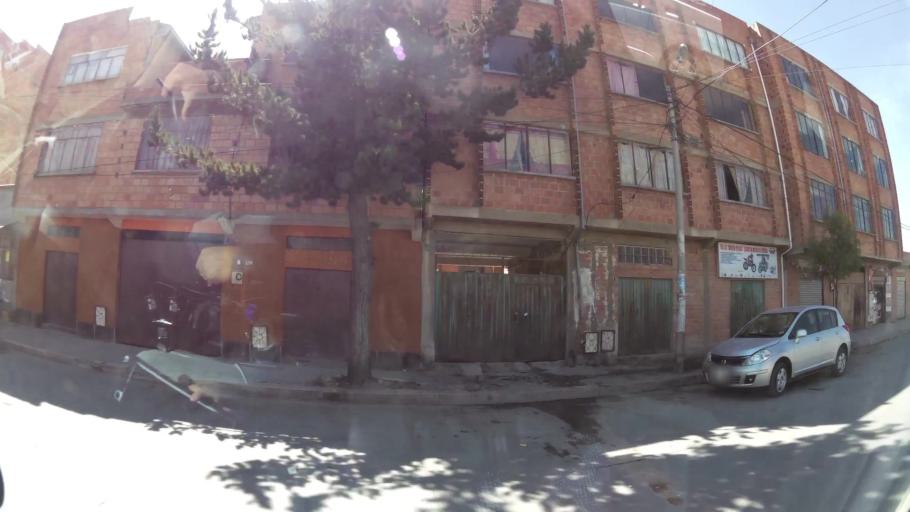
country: BO
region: La Paz
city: La Paz
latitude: -16.5309
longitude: -68.1591
